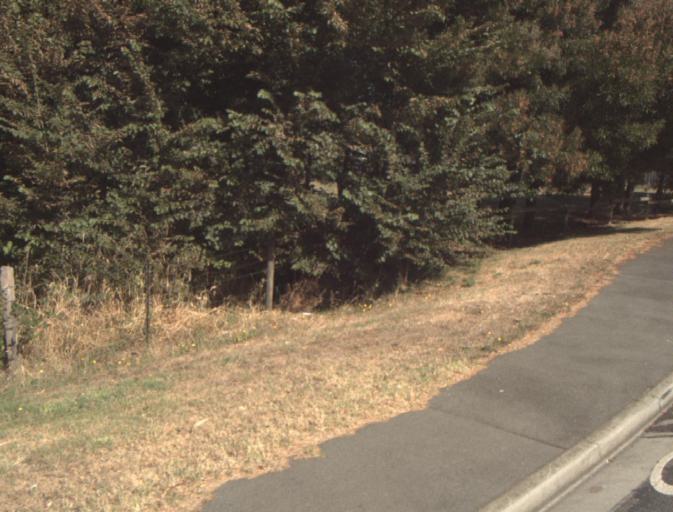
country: AU
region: Tasmania
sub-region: Launceston
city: Newstead
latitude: -41.4283
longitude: 147.1758
